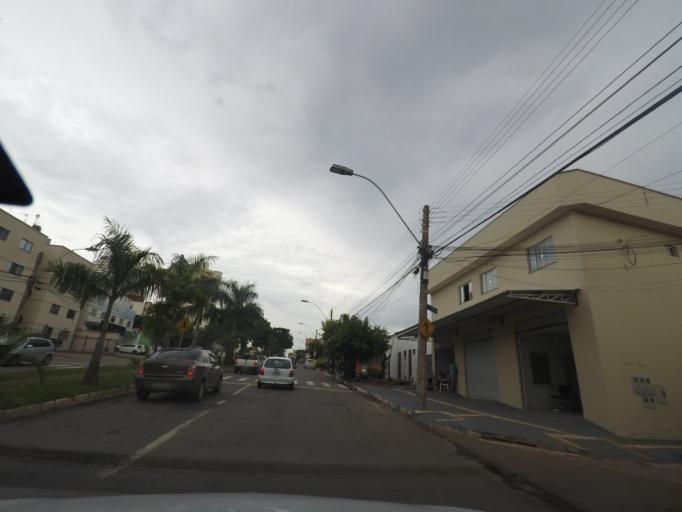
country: BR
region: Goias
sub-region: Goiania
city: Goiania
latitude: -16.7148
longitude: -49.2422
